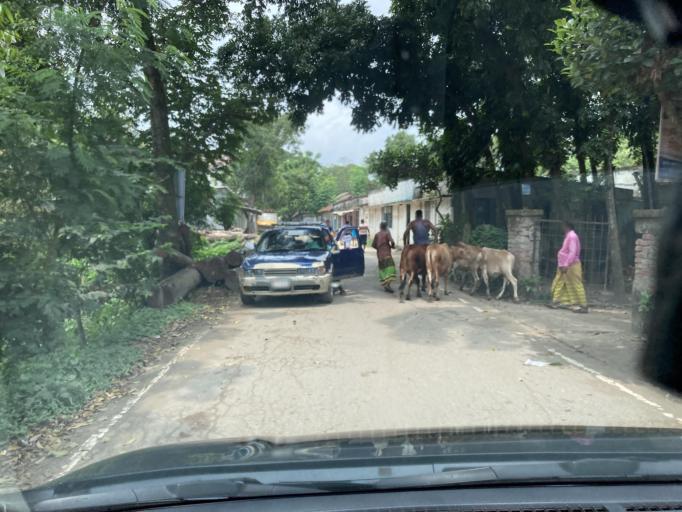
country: BD
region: Dhaka
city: Dohar
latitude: 23.7615
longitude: 90.1962
